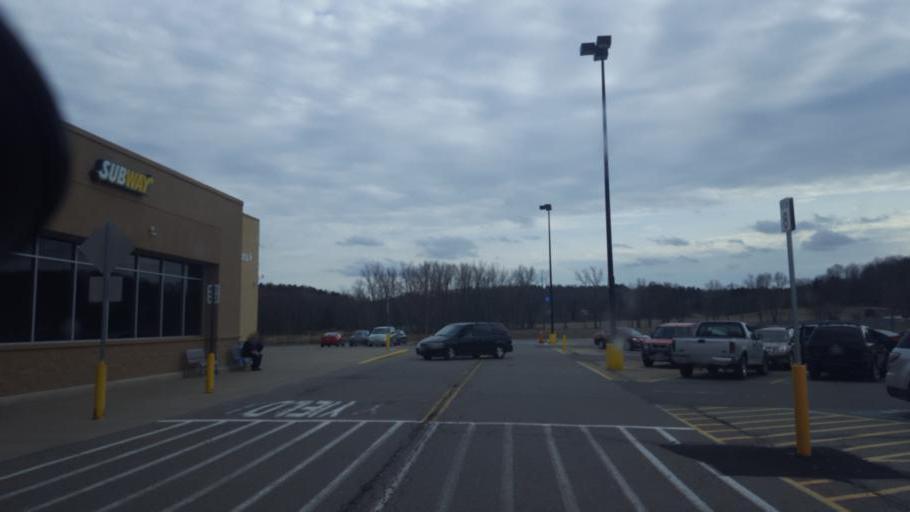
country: US
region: Ohio
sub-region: Richland County
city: Mansfield
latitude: 40.6913
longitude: -82.5088
